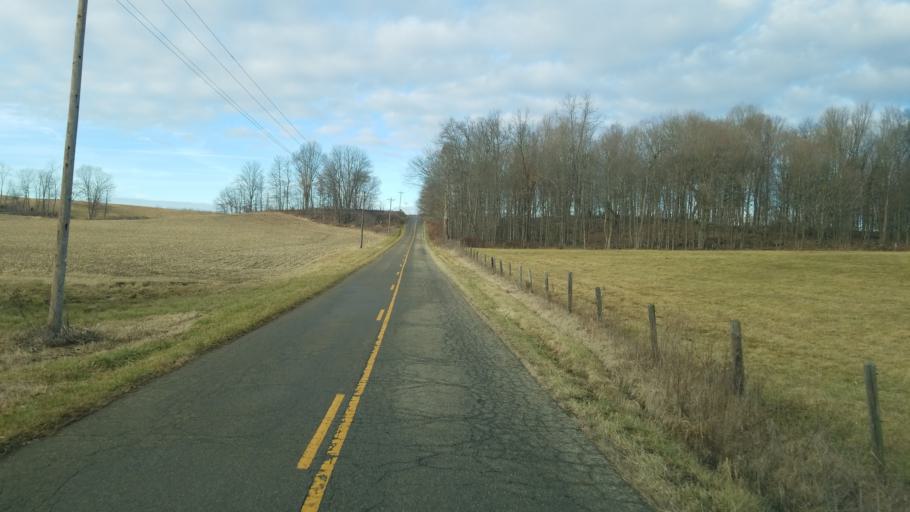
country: US
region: Ohio
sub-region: Knox County
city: Gambier
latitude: 40.3135
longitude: -82.3276
